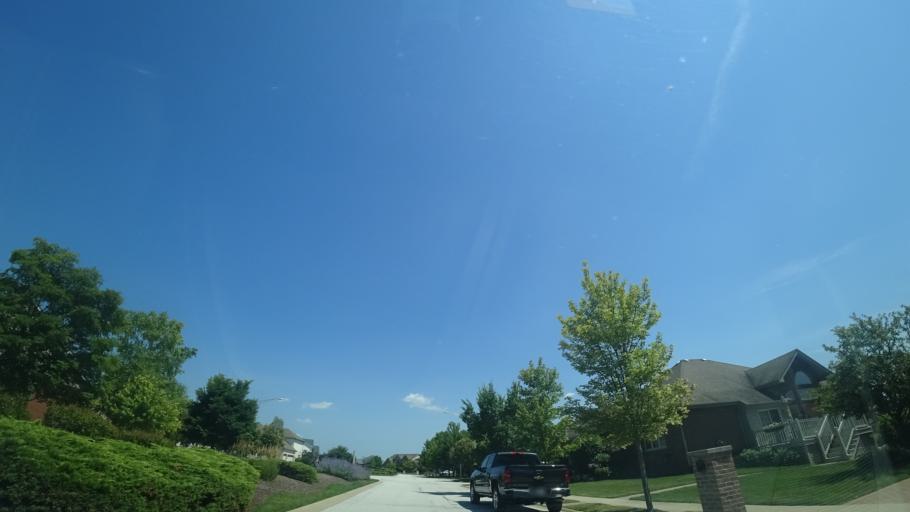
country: US
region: Illinois
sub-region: Will County
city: Mokena
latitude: 41.5609
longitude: -87.8888
